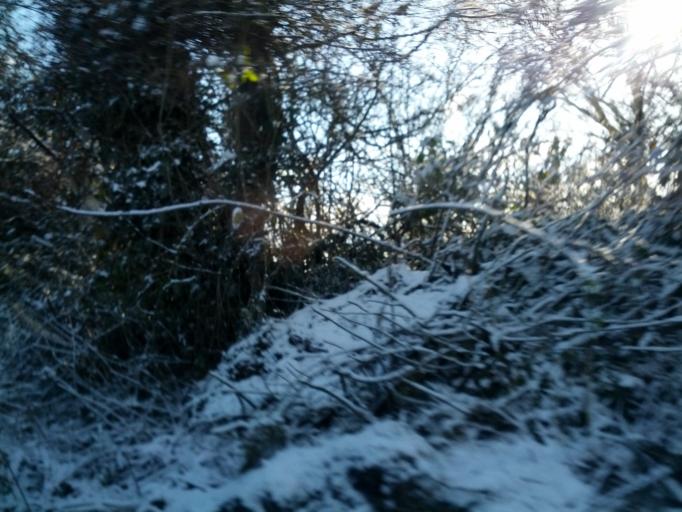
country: IE
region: Connaught
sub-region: County Galway
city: Athenry
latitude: 53.1890
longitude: -8.7886
